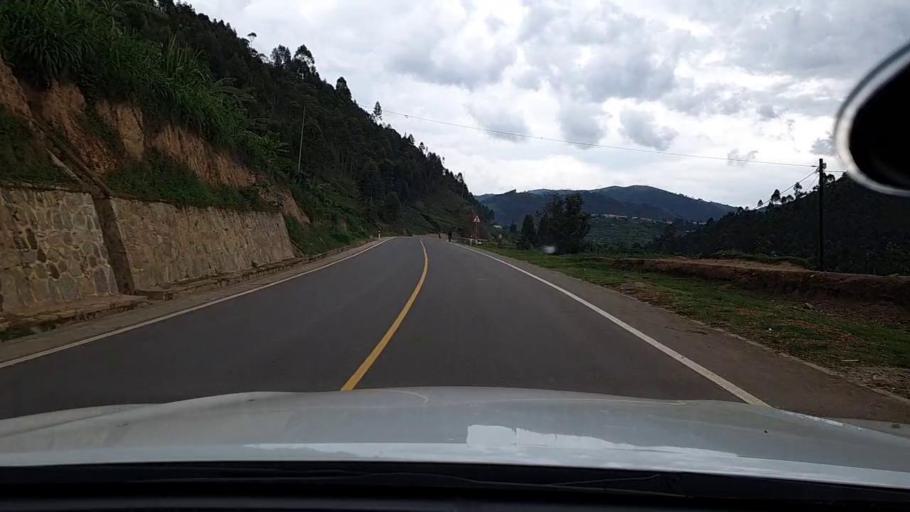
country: RW
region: Northern Province
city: Byumba
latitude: -1.6437
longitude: 29.9251
